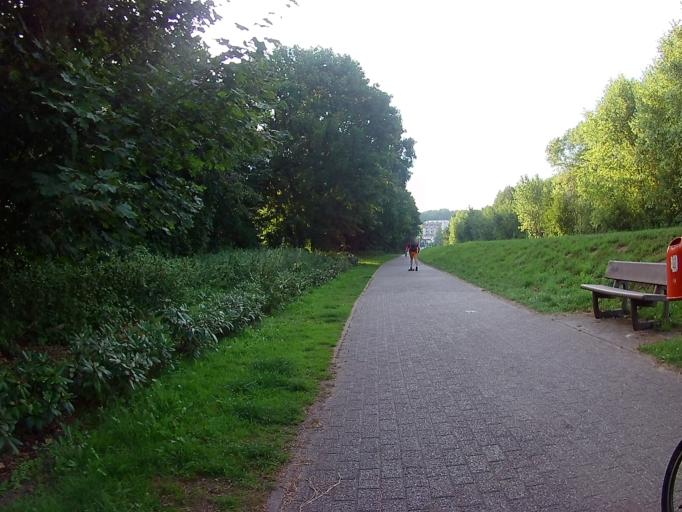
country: DE
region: Mecklenburg-Vorpommern
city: Loddin
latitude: 54.0381
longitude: 14.0335
